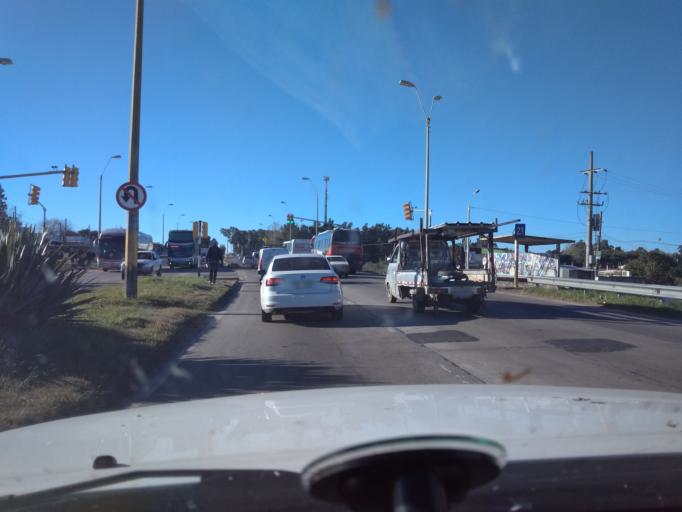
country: UY
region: Canelones
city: Joaquin Suarez
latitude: -34.7707
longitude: -56.0253
